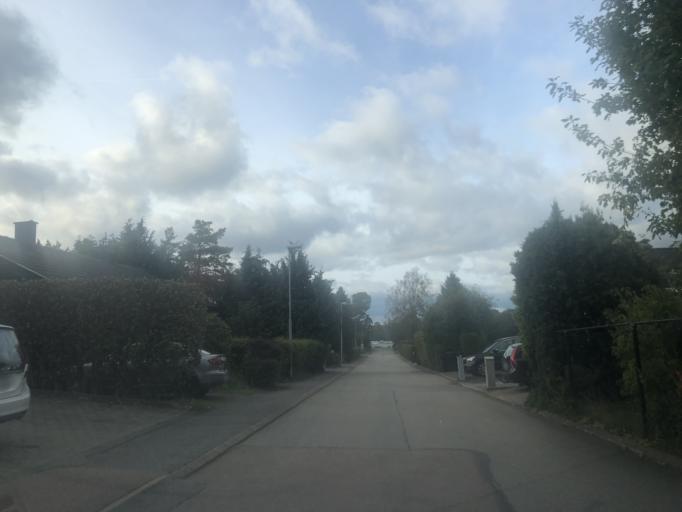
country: SE
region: Vaestra Goetaland
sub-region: Molndal
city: Moelndal
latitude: 57.6322
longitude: 11.9512
